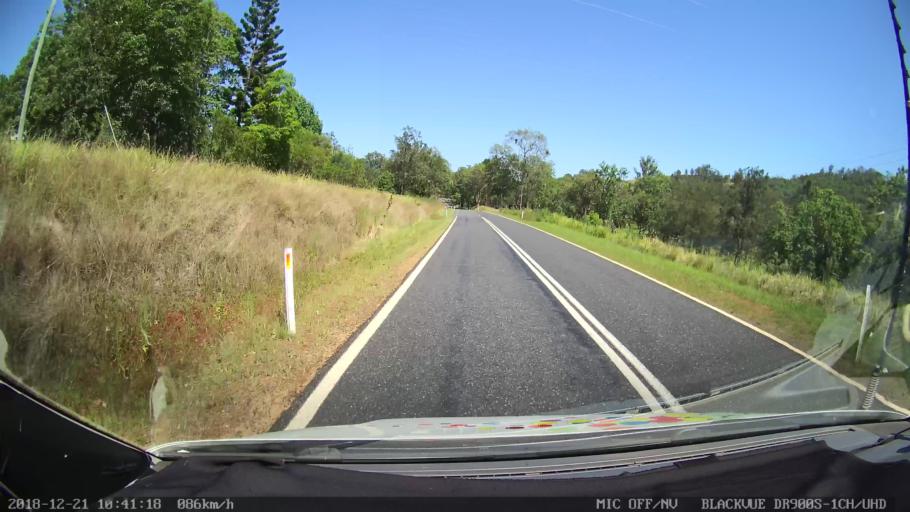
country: AU
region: New South Wales
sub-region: Clarence Valley
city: Gordon
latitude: -29.5921
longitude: 152.5765
